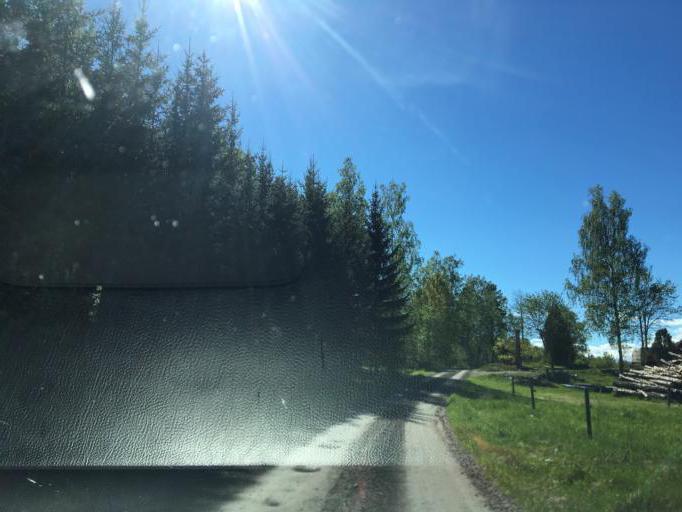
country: SE
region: Soedermanland
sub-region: Eskilstuna Kommun
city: Kvicksund
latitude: 59.3488
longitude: 16.3240
